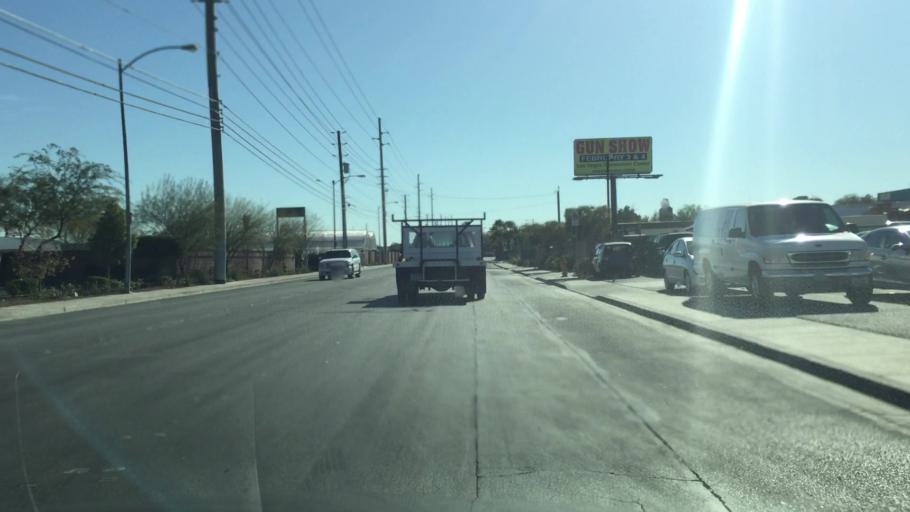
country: US
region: Nevada
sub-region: Clark County
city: Paradise
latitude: 36.1044
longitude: -115.1946
